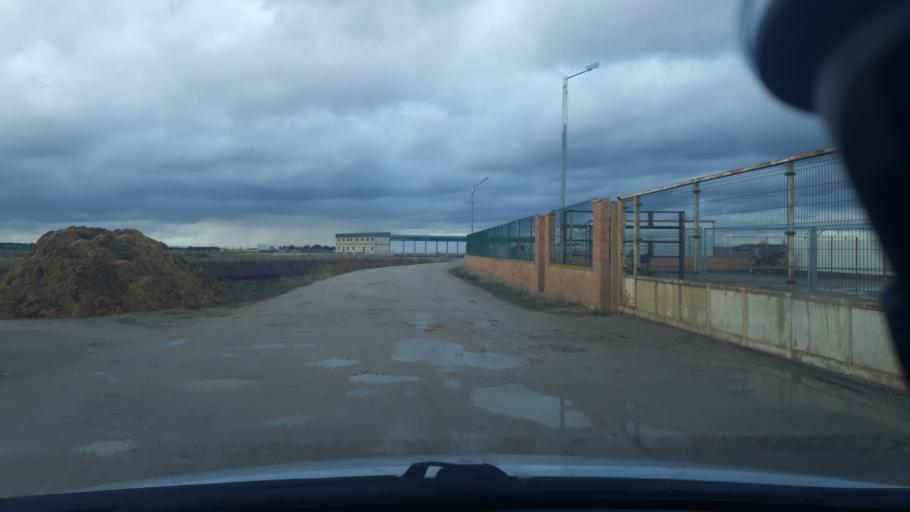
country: ES
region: Castille and Leon
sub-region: Provincia de Segovia
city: Sanchonuno
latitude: 41.2926
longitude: -4.3304
